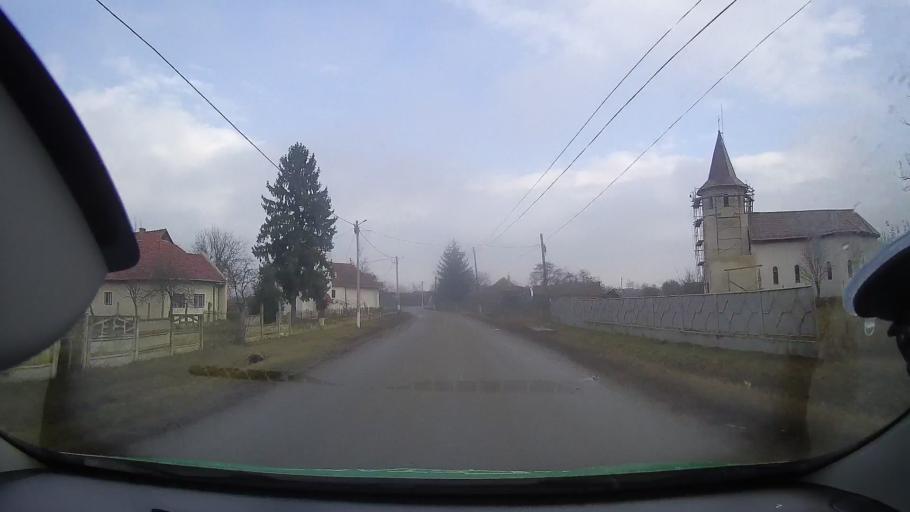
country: RO
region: Alba
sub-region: Comuna Noslac
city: Noslac
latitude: 46.4191
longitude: 23.9790
